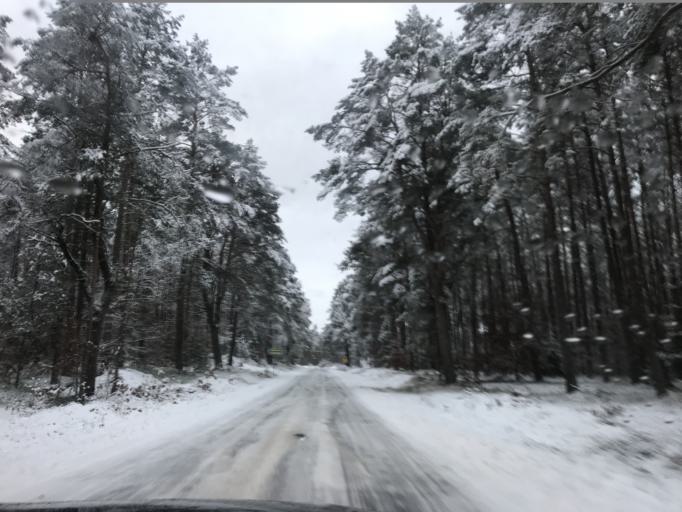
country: PL
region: Pomeranian Voivodeship
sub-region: Powiat bytowski
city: Czarna Dabrowka
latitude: 54.2745
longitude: 17.5871
